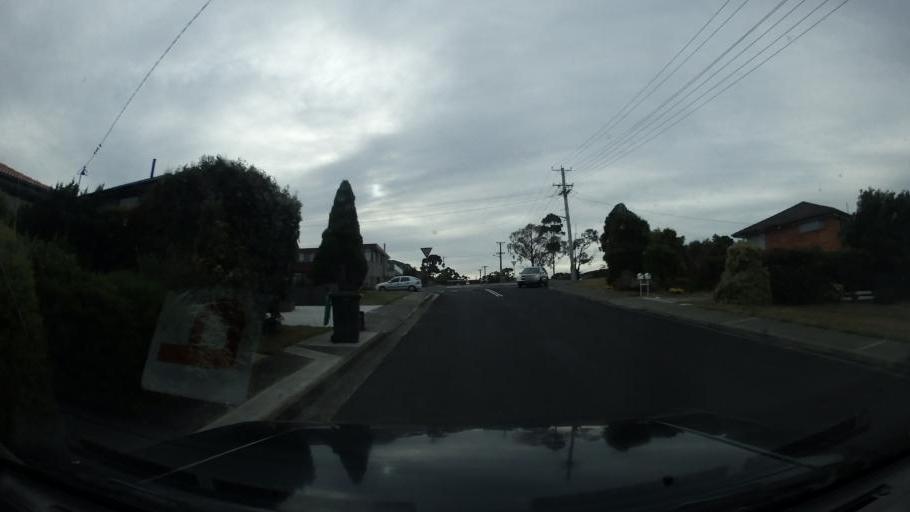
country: AU
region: Tasmania
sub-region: Clarence
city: Bellerive
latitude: -42.8701
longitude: 147.3759
